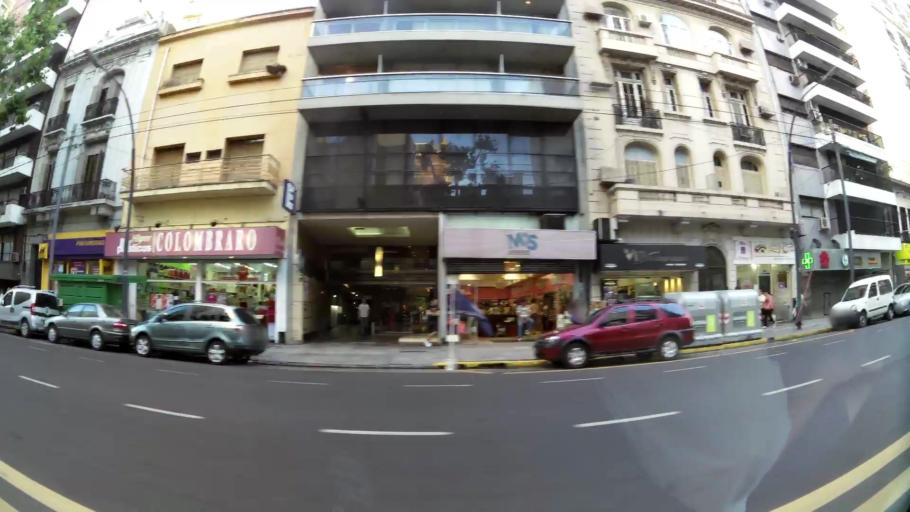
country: AR
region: Buenos Aires F.D.
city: Retiro
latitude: -34.5938
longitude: -58.4041
